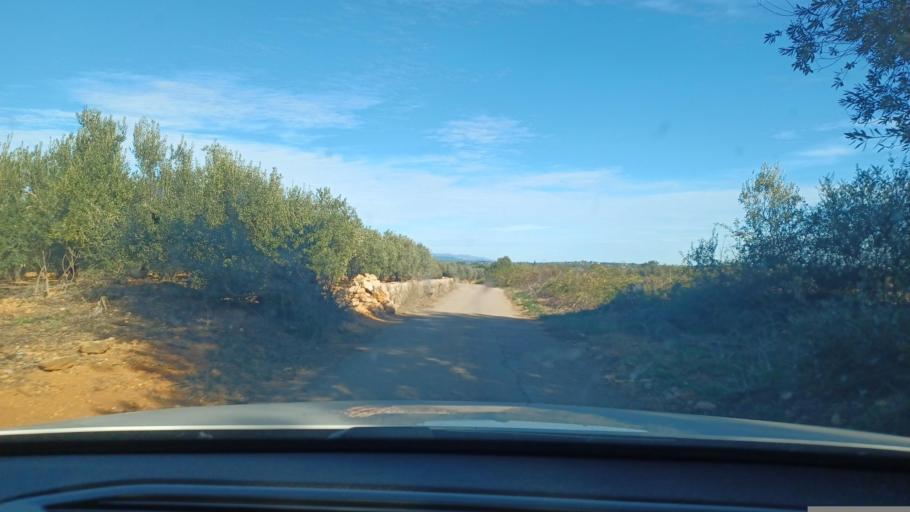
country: ES
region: Catalonia
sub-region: Provincia de Tarragona
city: Santa Barbara
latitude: 40.6885
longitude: 0.5030
